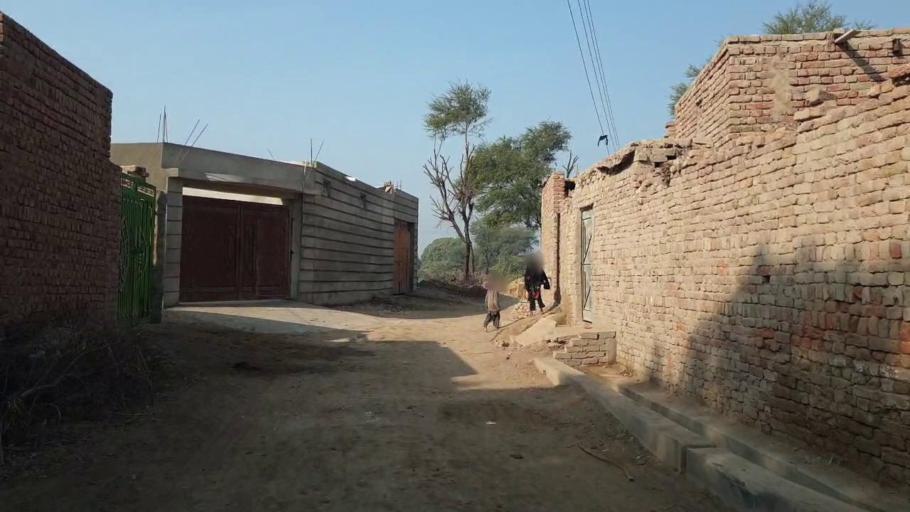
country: PK
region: Sindh
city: Matiari
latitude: 25.6753
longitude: 68.5017
